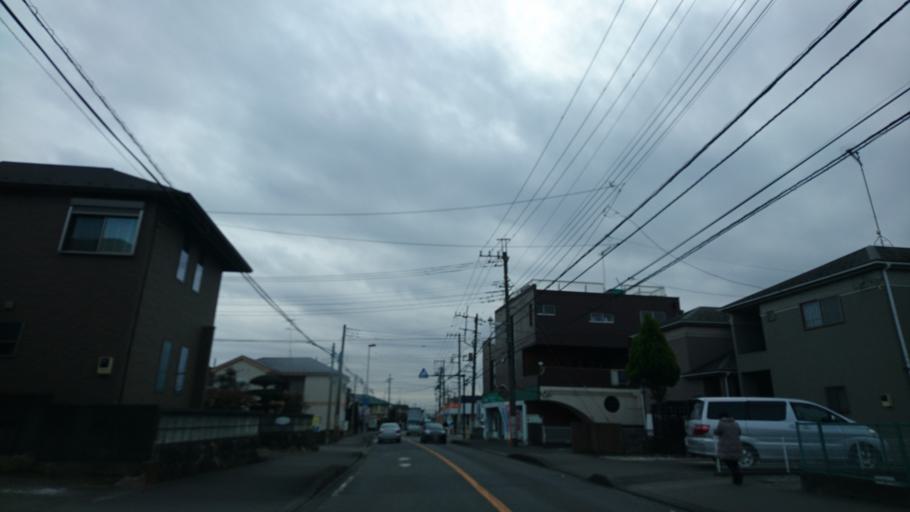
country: JP
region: Tokyo
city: Hachioji
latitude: 35.5790
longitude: 139.3337
